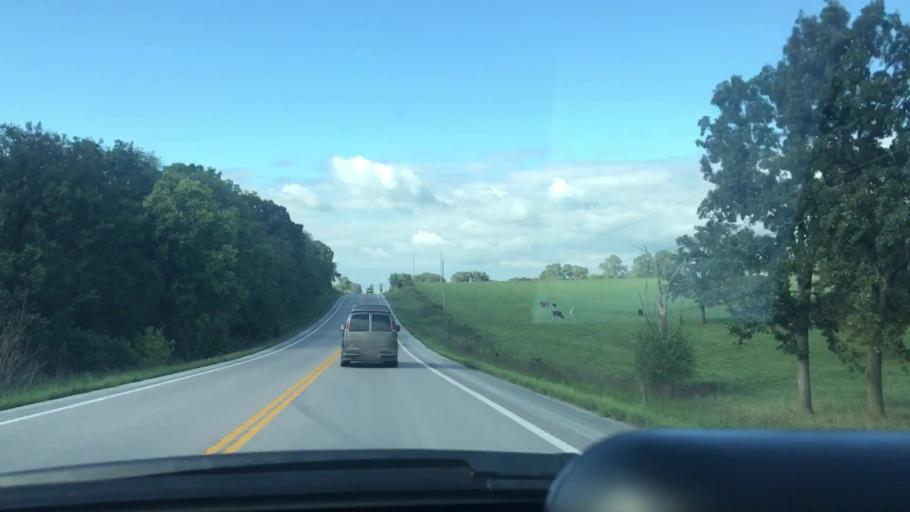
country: US
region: Missouri
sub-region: Hickory County
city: Hermitage
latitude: 37.9747
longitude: -93.2061
